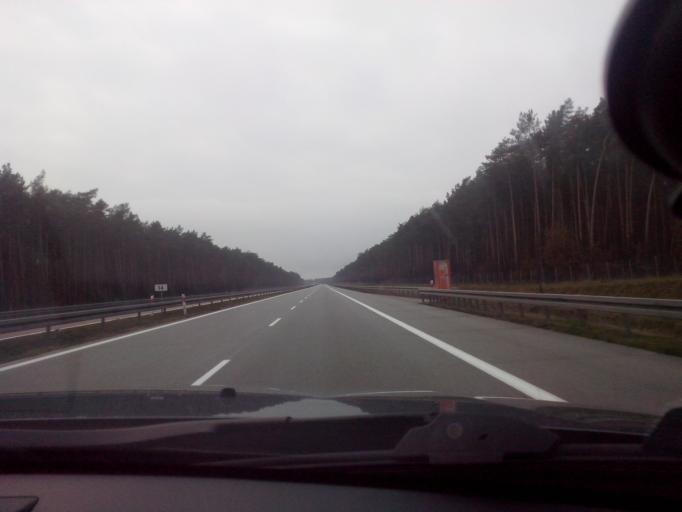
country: PL
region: Lubusz
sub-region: Powiat slubicki
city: Rzepin
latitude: 52.3354
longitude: 14.7807
